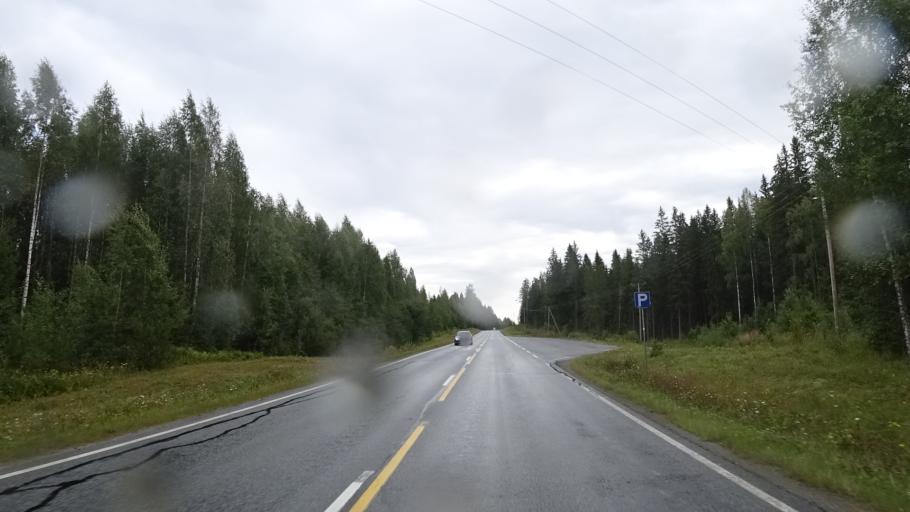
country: FI
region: North Karelia
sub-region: Keski-Karjala
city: Kesaelahti
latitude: 62.1071
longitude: 29.8106
